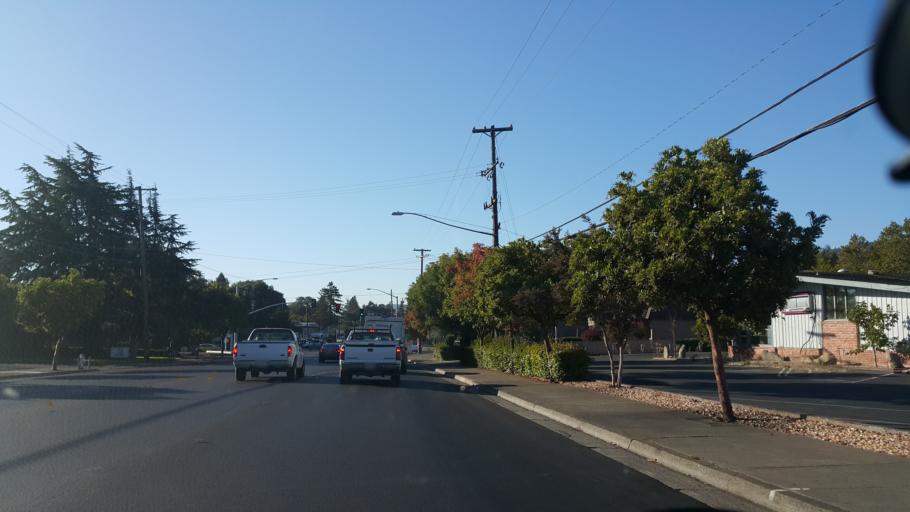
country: US
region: California
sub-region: Mendocino County
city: Ukiah
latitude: 39.1603
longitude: -123.2092
